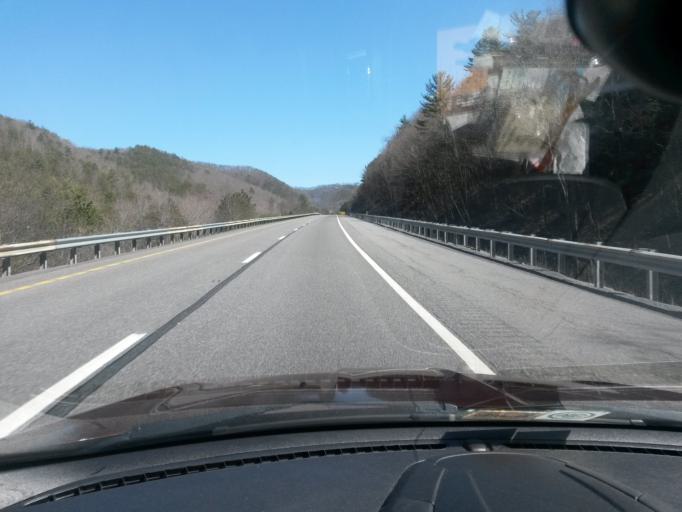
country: US
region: West Virginia
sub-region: Greenbrier County
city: White Sulphur Springs
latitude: 37.7880
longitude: -80.2507
